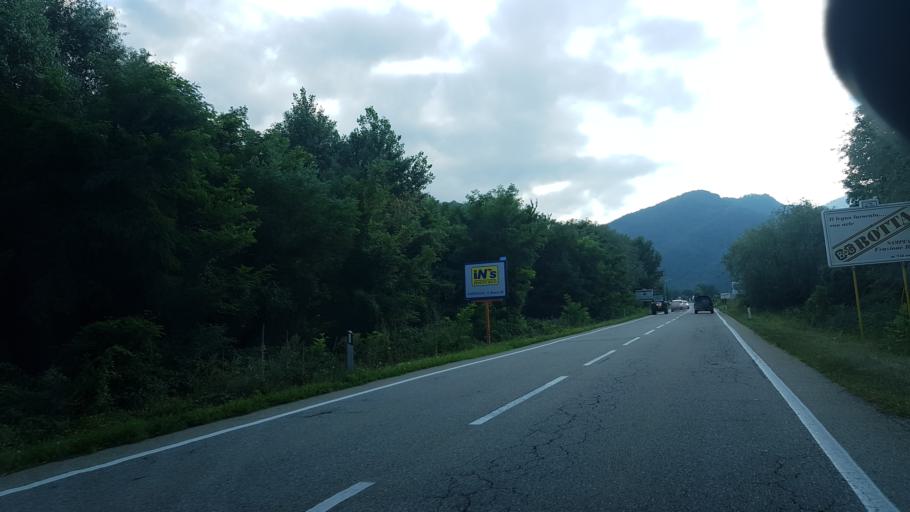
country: IT
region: Piedmont
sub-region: Provincia di Cuneo
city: Brossasco
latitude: 44.5681
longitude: 7.3763
